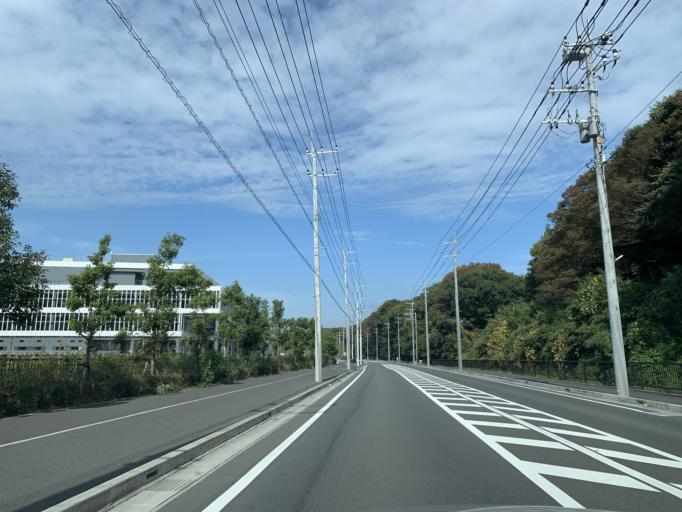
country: JP
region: Chiba
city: Nagareyama
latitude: 35.8996
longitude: 139.8954
